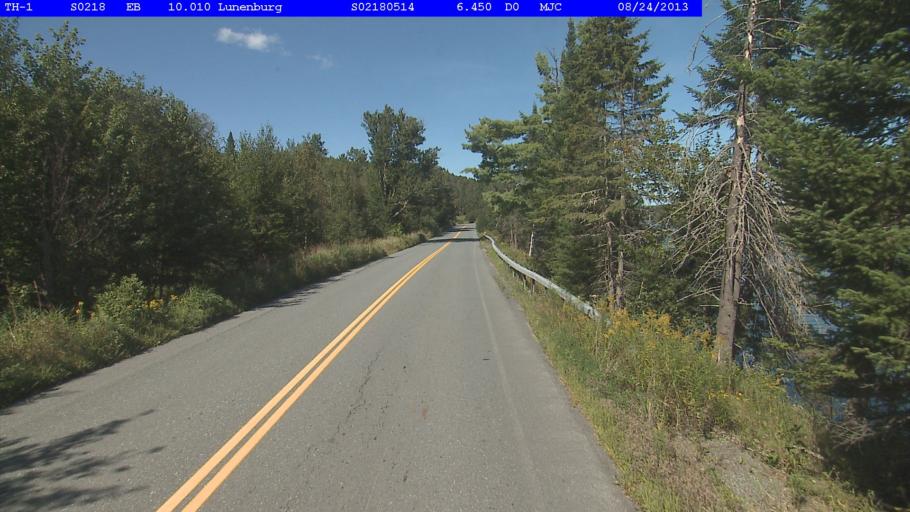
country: US
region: New Hampshire
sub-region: Coos County
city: Lancaster
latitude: 44.4550
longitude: -71.6572
